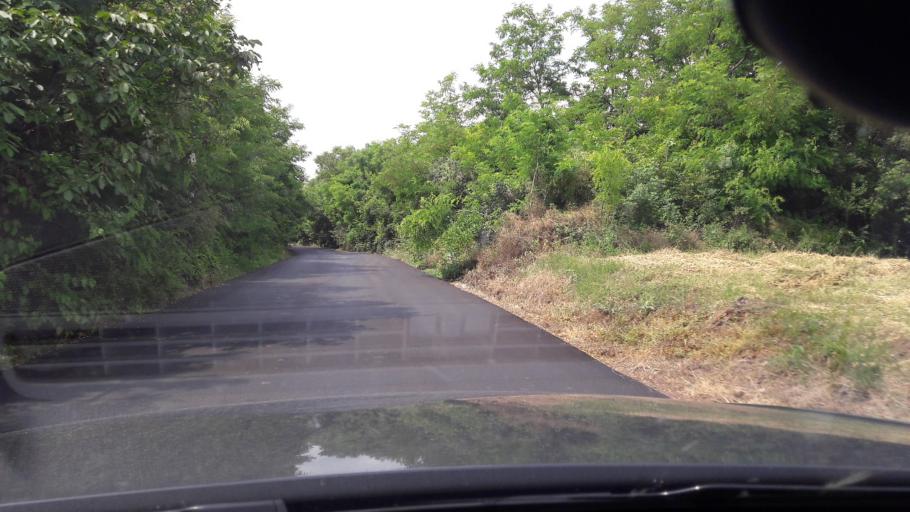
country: RS
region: Central Serbia
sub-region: Belgrade
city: Sopot
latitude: 44.6069
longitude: 20.6010
